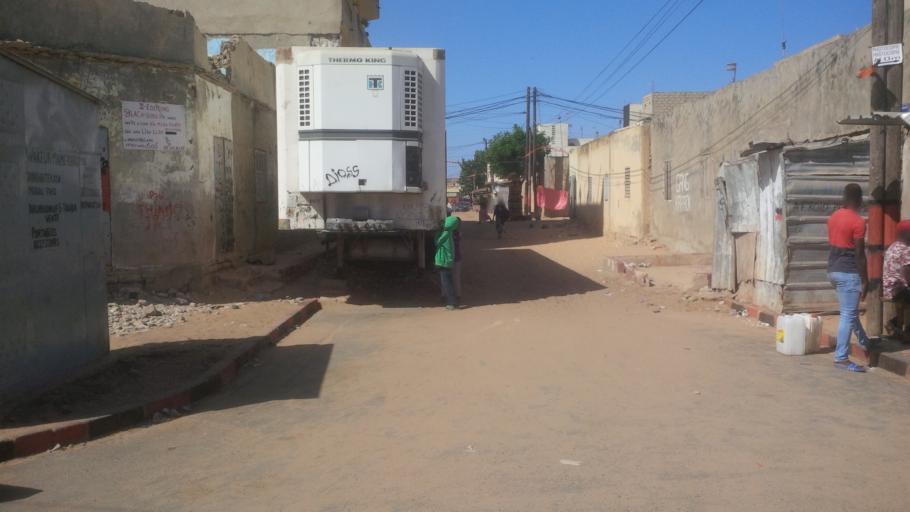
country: SN
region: Dakar
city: Pikine
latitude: 14.7770
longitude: -17.3723
